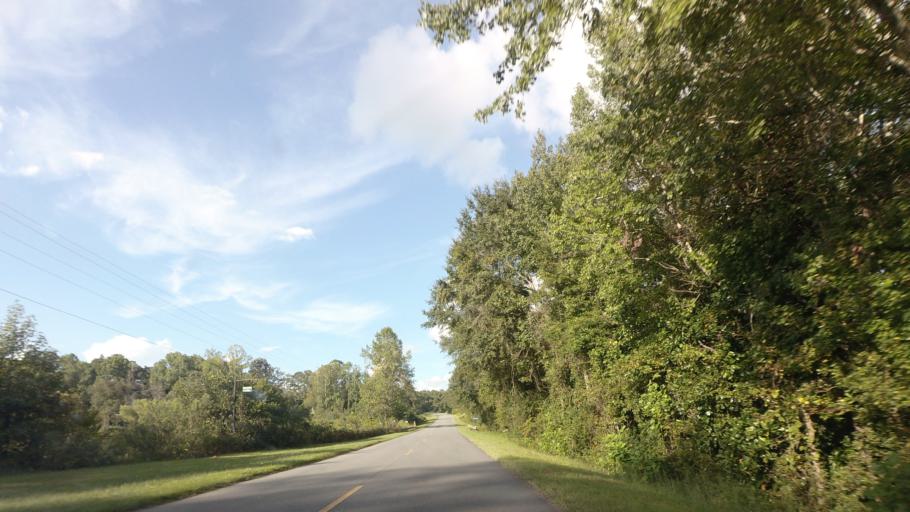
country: US
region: Georgia
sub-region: Pulaski County
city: Hawkinsville
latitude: 32.2919
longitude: -83.4928
